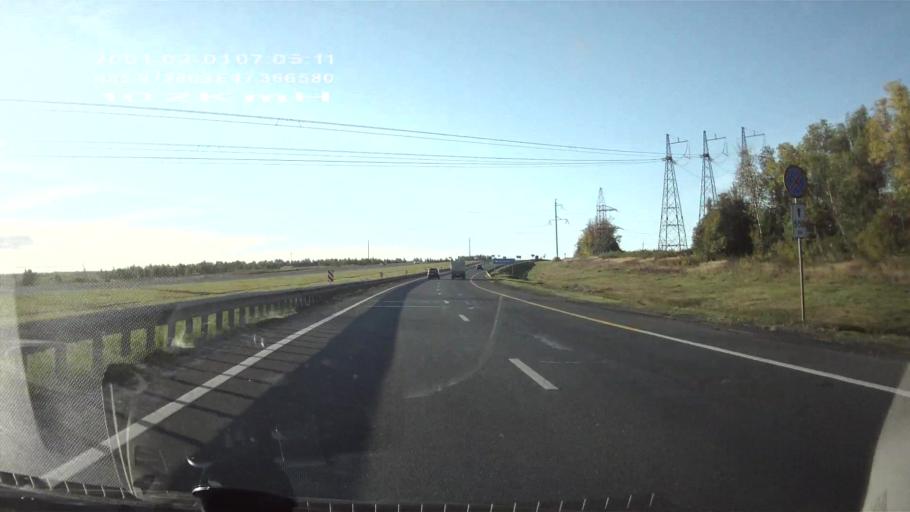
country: RU
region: Chuvashia
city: Kugesi
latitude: 55.9718
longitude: 47.3650
